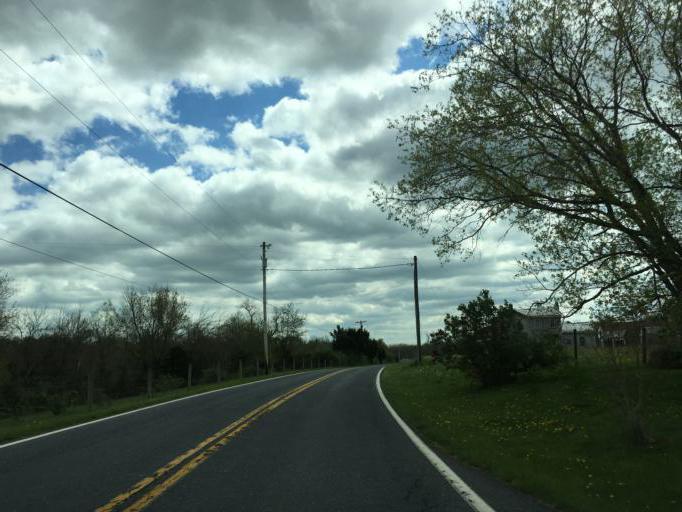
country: US
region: Maryland
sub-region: Frederick County
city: Thurmont
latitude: 39.5885
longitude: -77.3926
